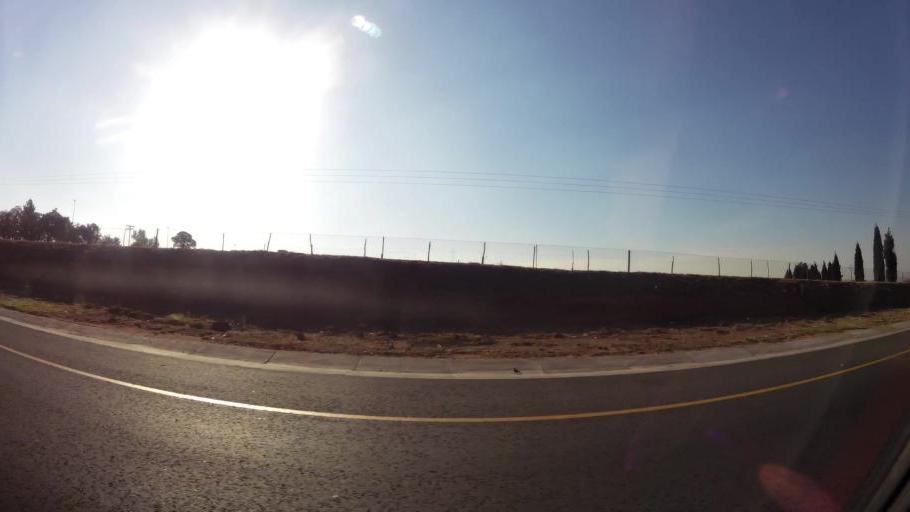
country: ZA
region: Gauteng
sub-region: West Rand District Municipality
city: Muldersdriseloop
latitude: -26.0118
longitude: 27.8816
